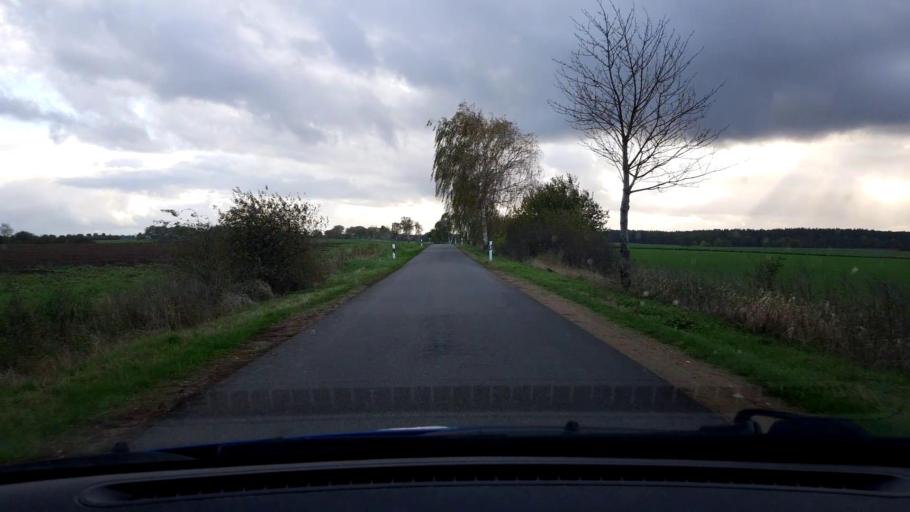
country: DE
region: Lower Saxony
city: Reinstorf
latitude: 53.2633
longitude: 10.5657
